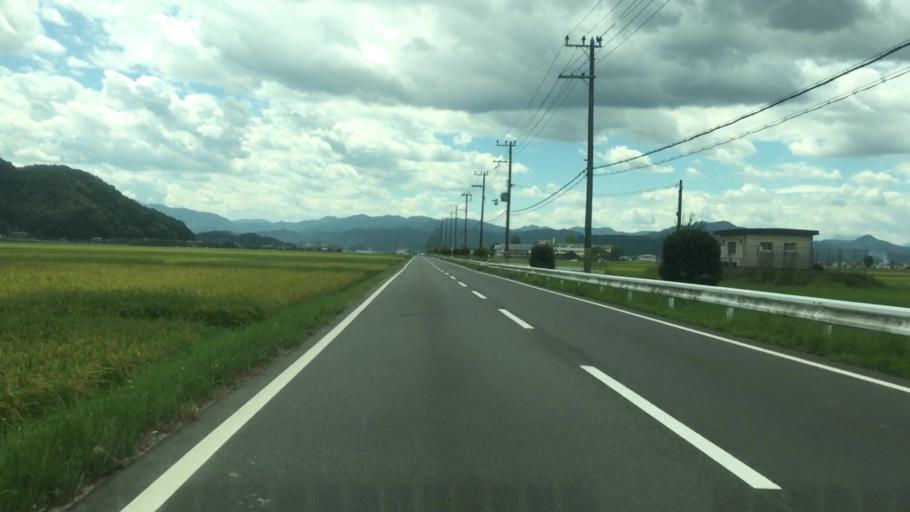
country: JP
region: Hyogo
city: Toyooka
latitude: 35.5378
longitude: 134.8397
